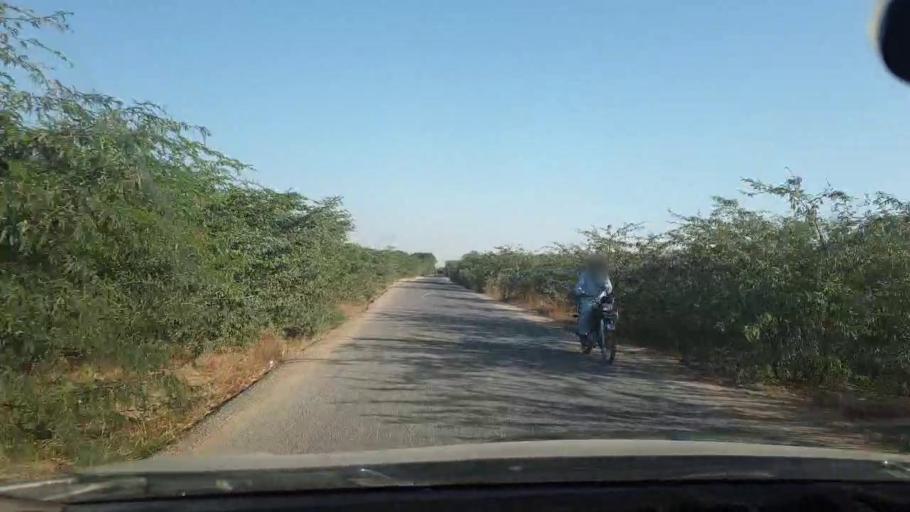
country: PK
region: Sindh
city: Malir Cantonment
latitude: 25.1472
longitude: 67.1879
